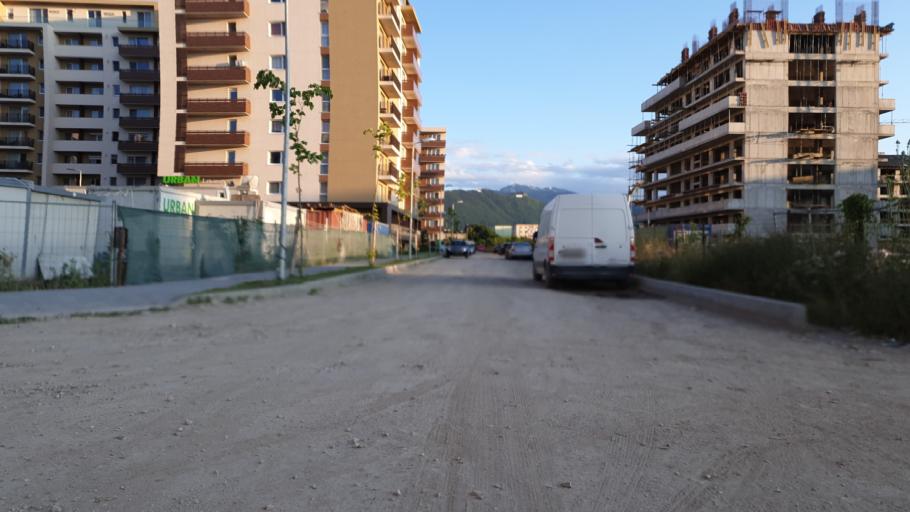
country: RO
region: Brasov
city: Brasov
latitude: 45.6737
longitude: 25.6092
